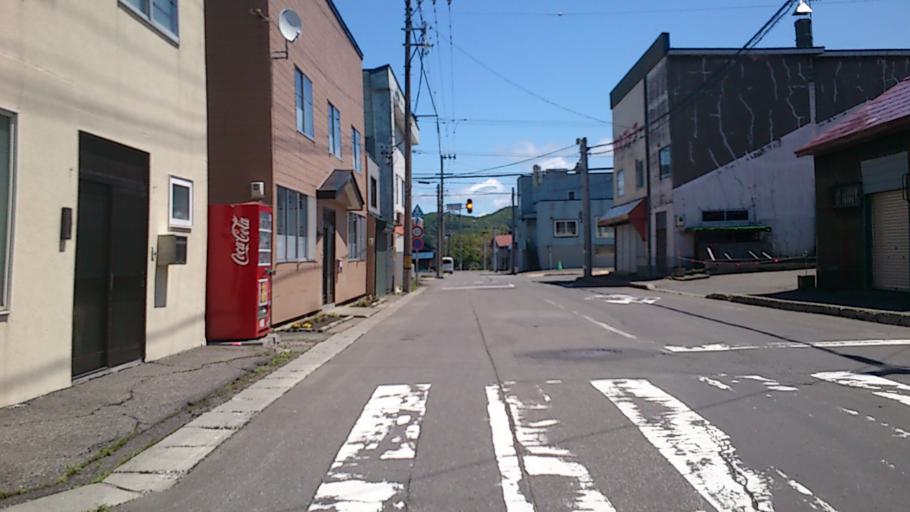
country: JP
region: Hokkaido
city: Rumoi
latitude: 43.9461
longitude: 141.6329
